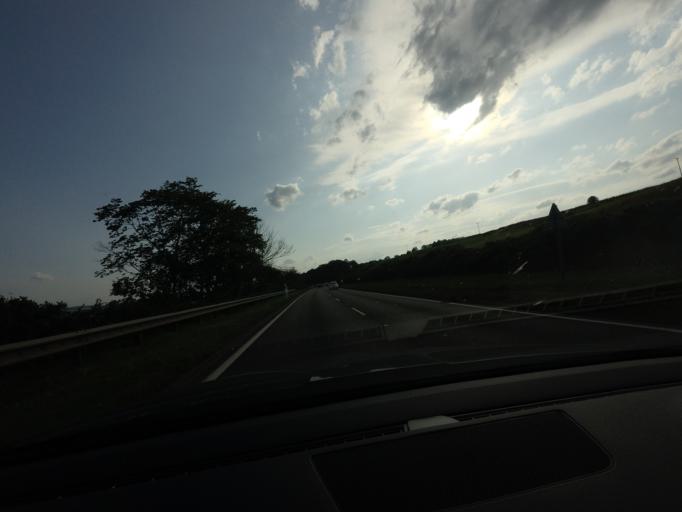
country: GB
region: Scotland
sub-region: Highland
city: Evanton
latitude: 57.6373
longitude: -4.3549
